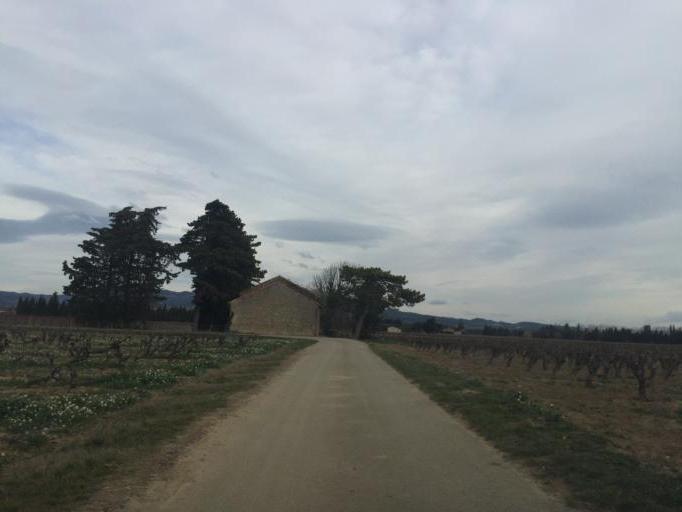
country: FR
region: Provence-Alpes-Cote d'Azur
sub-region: Departement du Vaucluse
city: Violes
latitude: 44.1555
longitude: 4.9289
